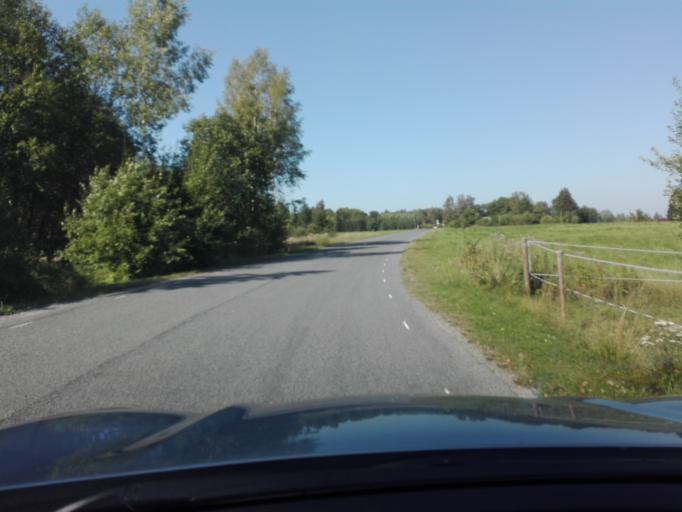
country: EE
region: Raplamaa
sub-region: Rapla vald
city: Rapla
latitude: 59.0666
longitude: 24.7996
